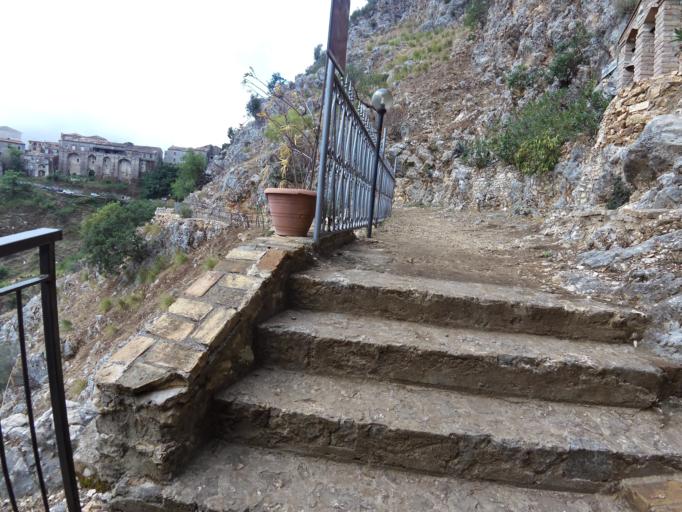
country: IT
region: Calabria
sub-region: Provincia di Reggio Calabria
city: Stilo
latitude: 38.4823
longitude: 16.4692
